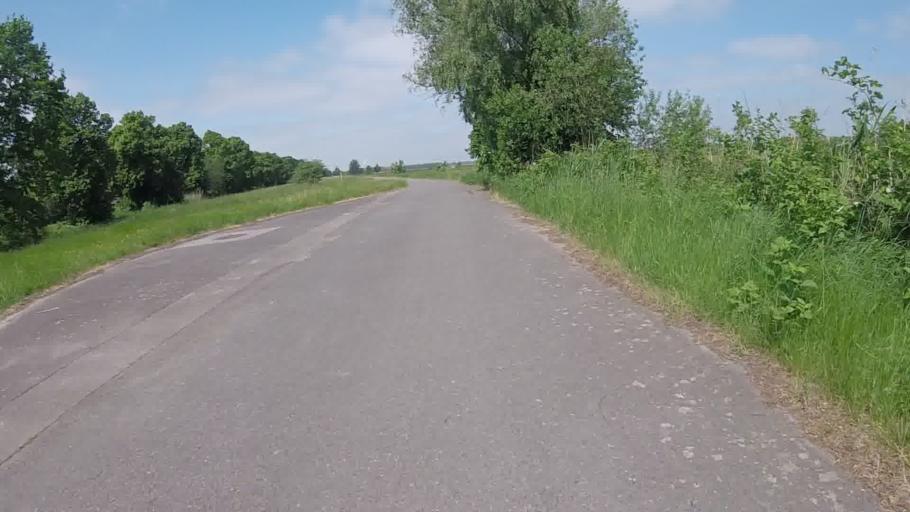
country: DE
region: Schleswig-Holstein
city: Oststeinbek
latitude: 53.4996
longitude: 10.1306
